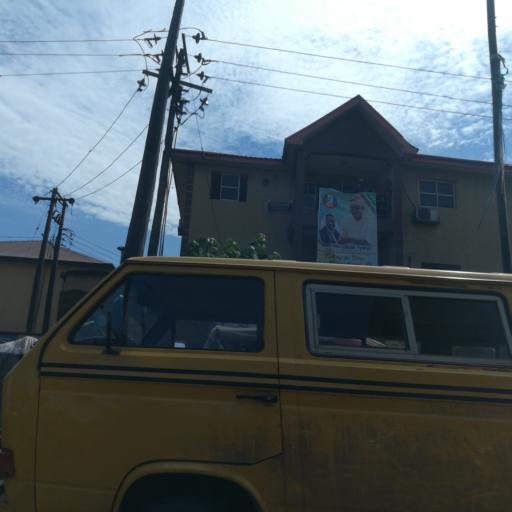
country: NG
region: Lagos
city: Lagos
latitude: 6.4633
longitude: 3.3925
